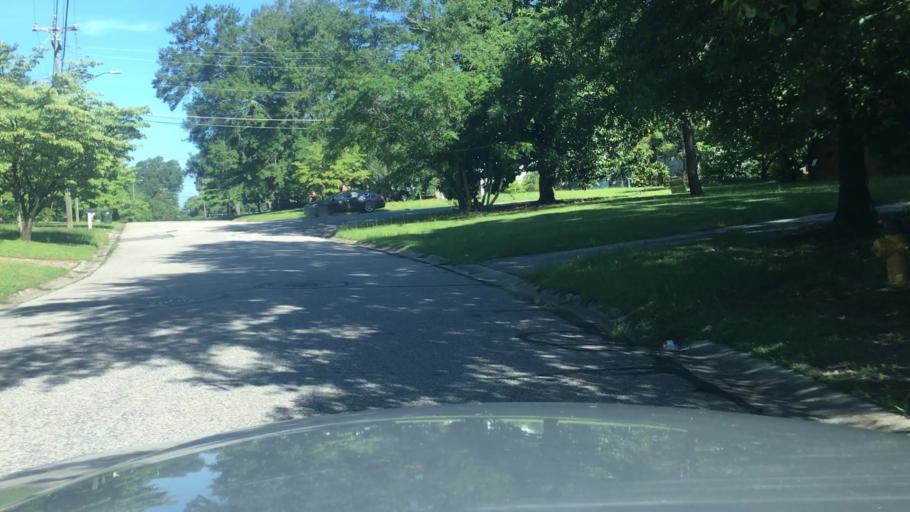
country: US
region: North Carolina
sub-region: Cumberland County
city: Fayetteville
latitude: 35.1354
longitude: -78.8894
